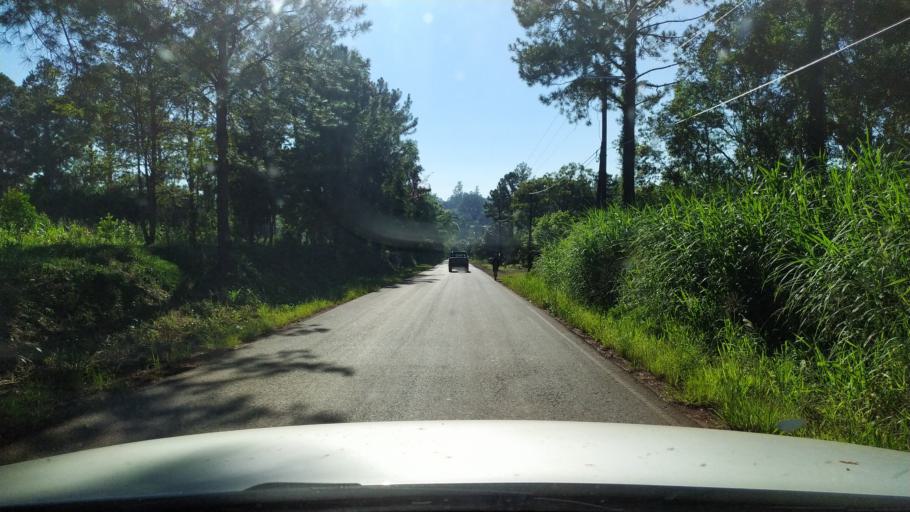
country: AR
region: Misiones
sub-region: Departamento de Montecarlo
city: Montecarlo
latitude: -26.5904
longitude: -54.7187
